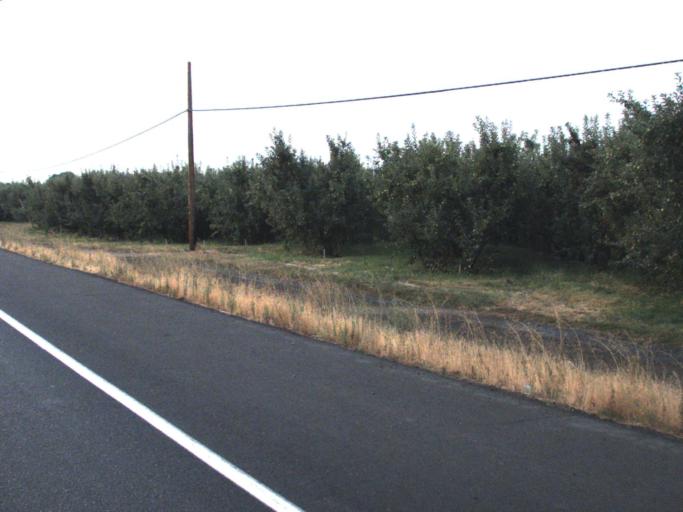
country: US
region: Washington
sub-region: Yakima County
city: Wapato
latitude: 46.4753
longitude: -120.4452
